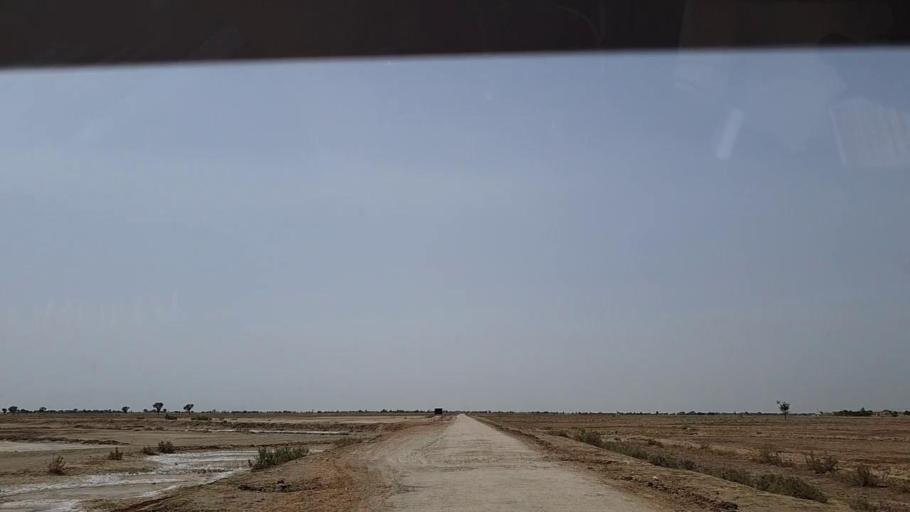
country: PK
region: Sindh
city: Johi
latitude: 26.7437
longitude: 67.6290
